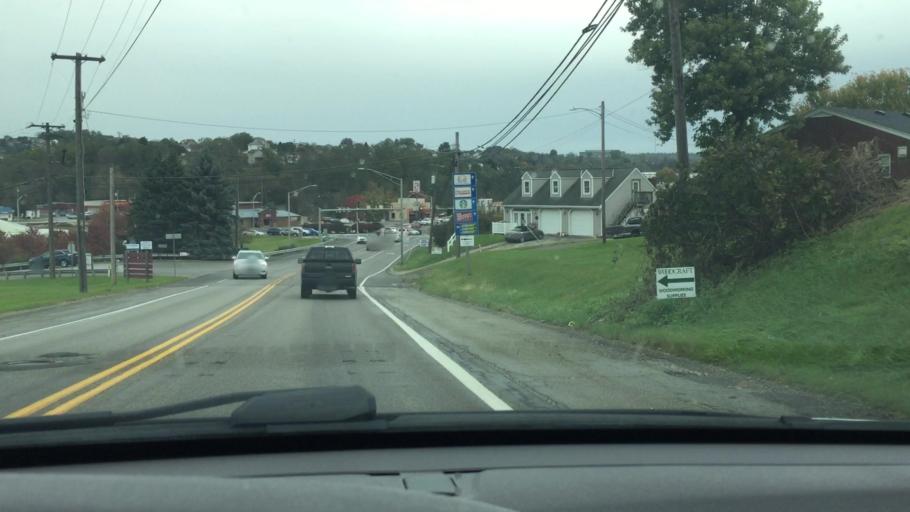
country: US
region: Pennsylvania
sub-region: Washington County
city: Canonsburg
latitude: 40.2600
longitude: -80.1751
